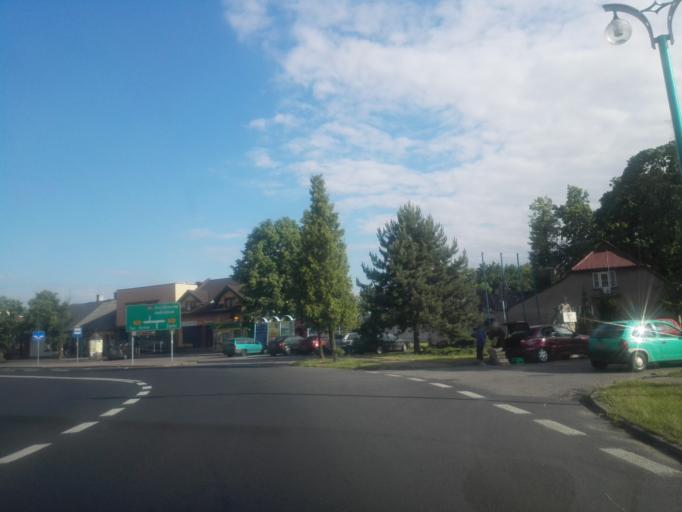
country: PL
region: Silesian Voivodeship
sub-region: Powiat czestochowski
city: Potok Zloty
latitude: 50.7223
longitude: 19.4350
